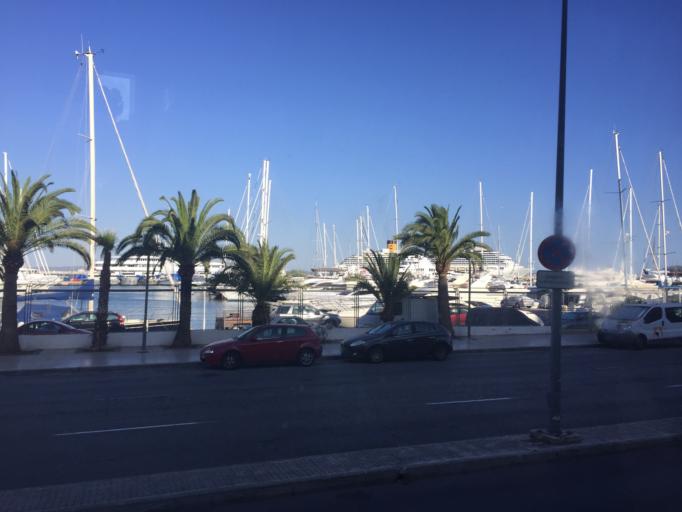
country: ES
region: Balearic Islands
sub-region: Illes Balears
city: Palma
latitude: 39.5595
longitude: 2.6266
